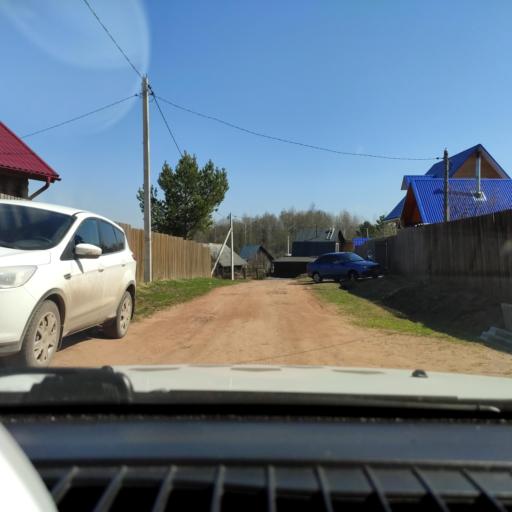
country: RU
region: Perm
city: Perm
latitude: 58.0673
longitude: 56.3752
